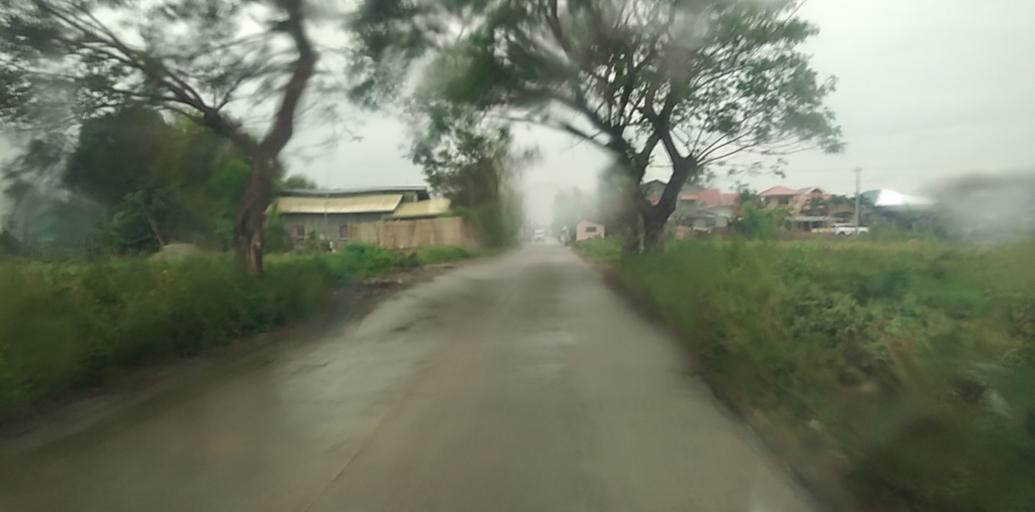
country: PH
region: Central Luzon
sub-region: Province of Pampanga
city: Anao
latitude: 15.1456
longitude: 120.7041
